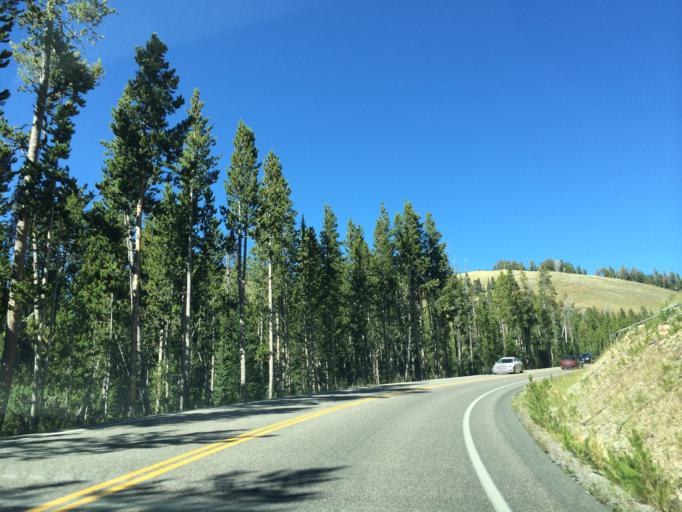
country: US
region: Montana
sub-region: Gallatin County
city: West Yellowstone
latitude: 44.7553
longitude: -110.4825
